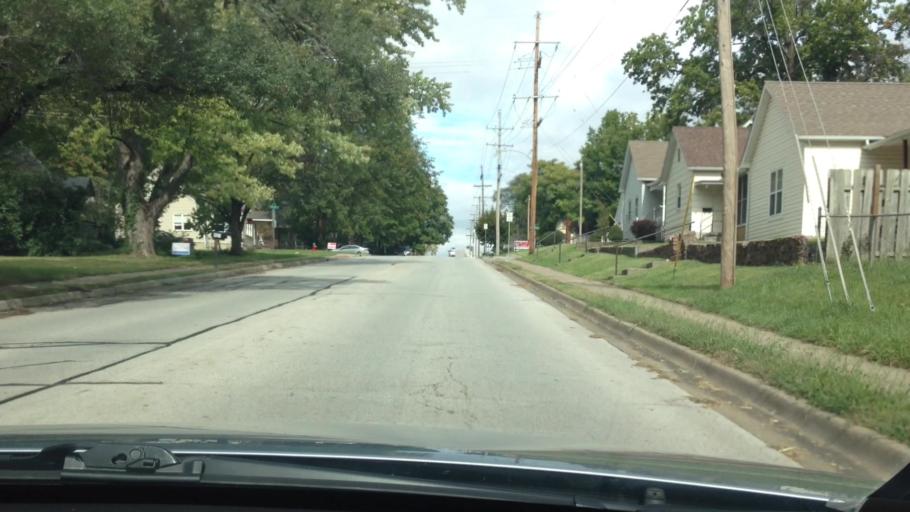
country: US
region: Kansas
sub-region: Leavenworth County
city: Leavenworth
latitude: 39.3252
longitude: -94.9282
